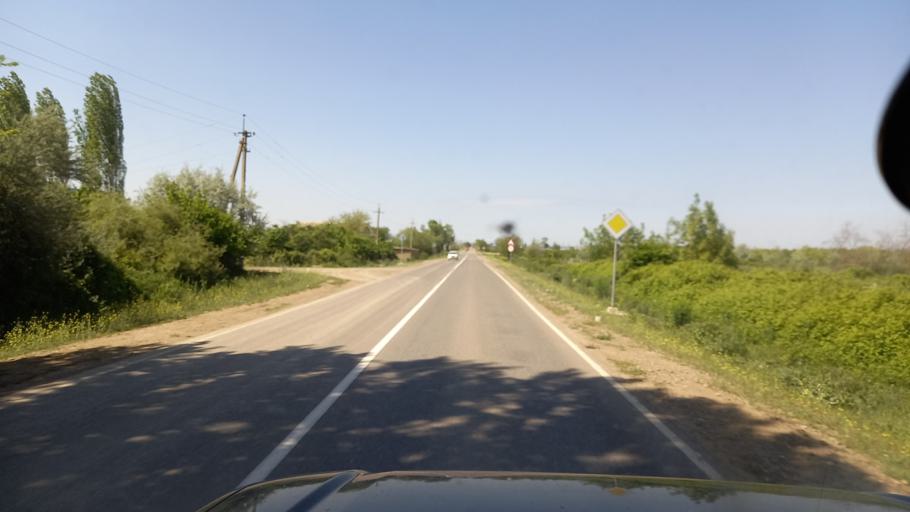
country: RU
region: Dagestan
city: Novaya Maka
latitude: 41.8171
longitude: 48.4025
